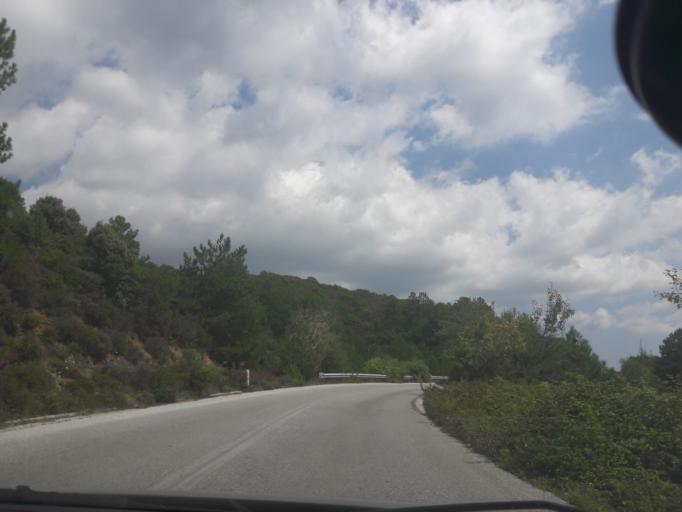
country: GR
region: Central Macedonia
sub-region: Nomos Chalkidikis
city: Polygyros
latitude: 40.3532
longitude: 23.4833
